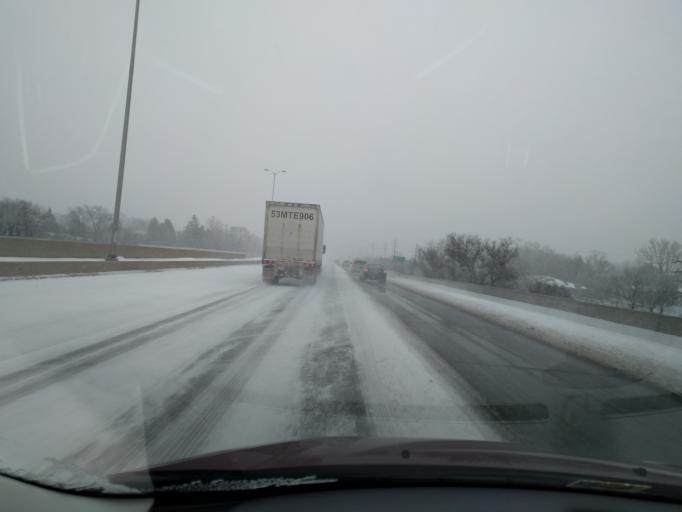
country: US
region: Wisconsin
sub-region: Waukesha County
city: Butler
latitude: 43.1350
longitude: -88.0322
